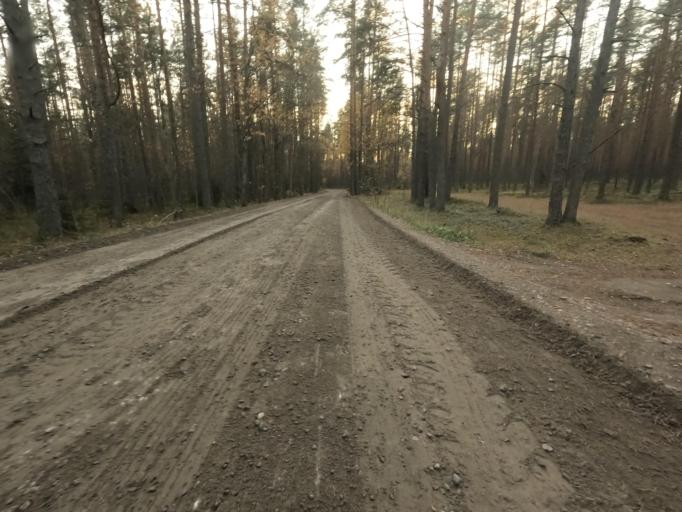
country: RU
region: St.-Petersburg
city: Repino
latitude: 60.1905
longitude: 29.8845
